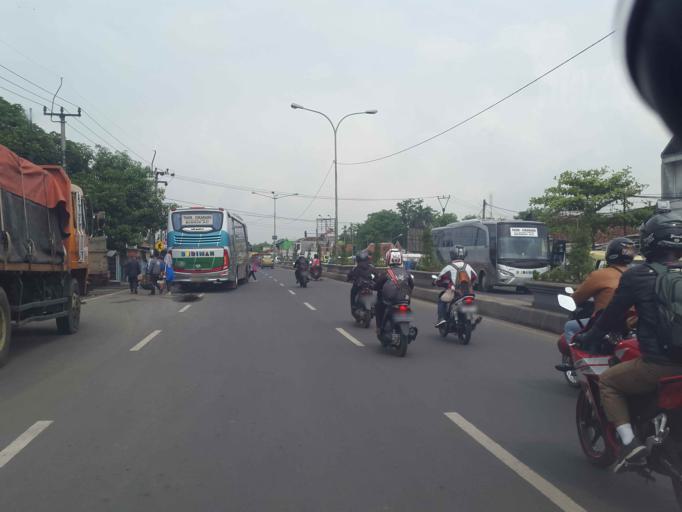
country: ID
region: West Java
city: Rengasdengklok
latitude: -6.2758
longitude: 107.2719
